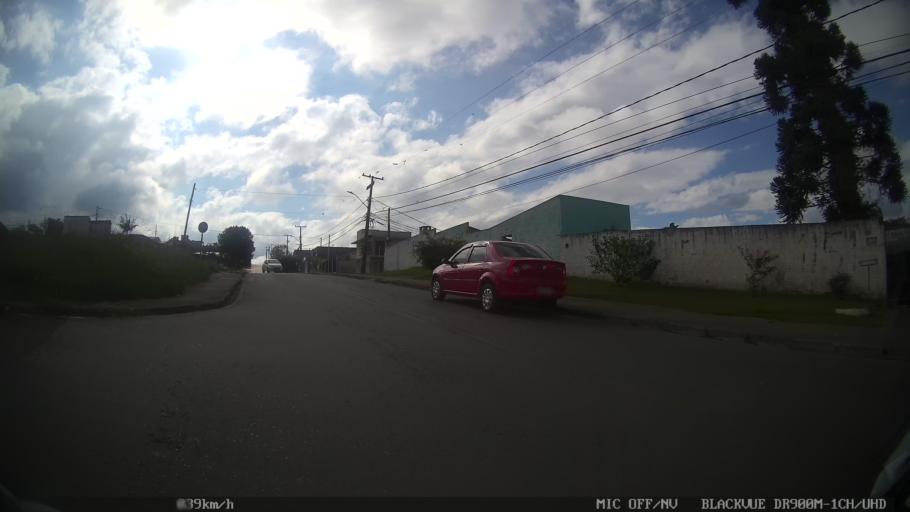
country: BR
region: Parana
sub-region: Colombo
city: Colombo
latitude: -25.3566
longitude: -49.1852
